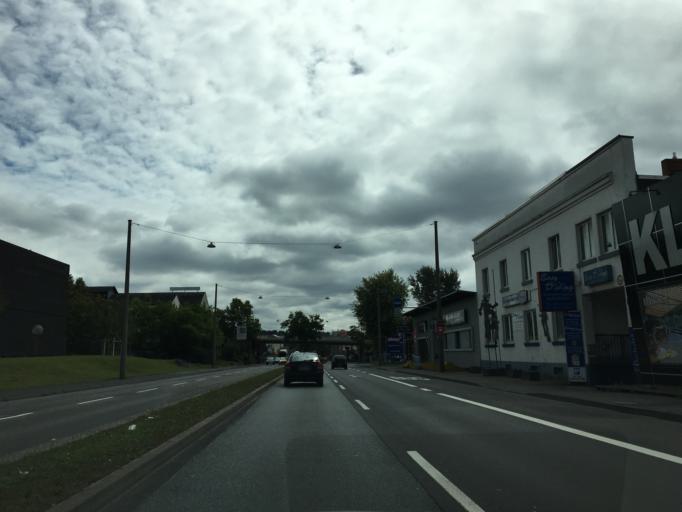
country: DE
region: Hesse
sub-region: Regierungsbezirk Darmstadt
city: Wiesbaden
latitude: 50.0598
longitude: 8.2541
